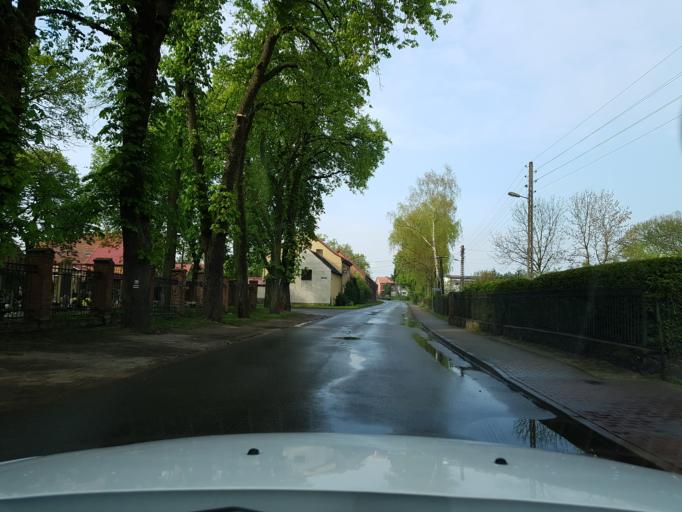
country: PL
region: West Pomeranian Voivodeship
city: Trzcinsko Zdroj
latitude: 52.9693
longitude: 14.6055
